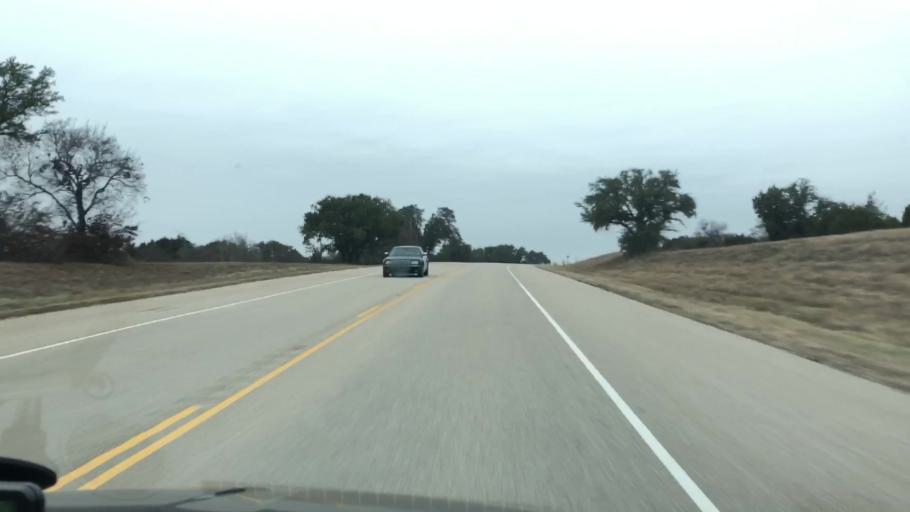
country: US
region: Texas
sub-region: Hamilton County
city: Hamilton
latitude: 31.5441
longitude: -98.1588
